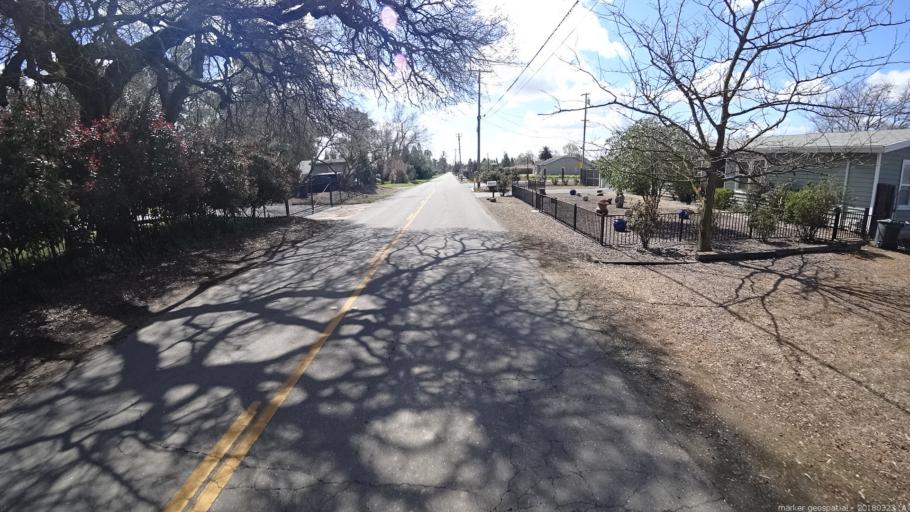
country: US
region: California
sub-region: Sacramento County
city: Rio Linda
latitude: 38.6893
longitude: -121.4245
